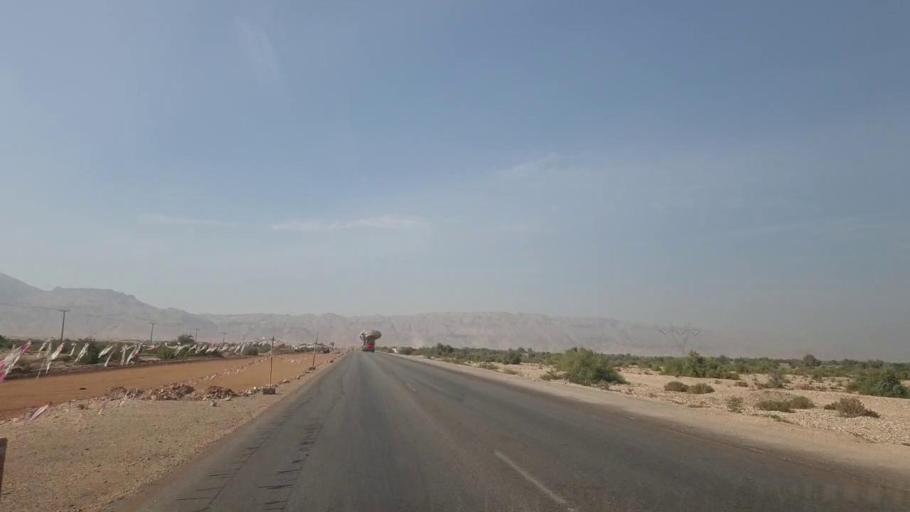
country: PK
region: Sindh
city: Sehwan
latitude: 26.2141
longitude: 67.9181
